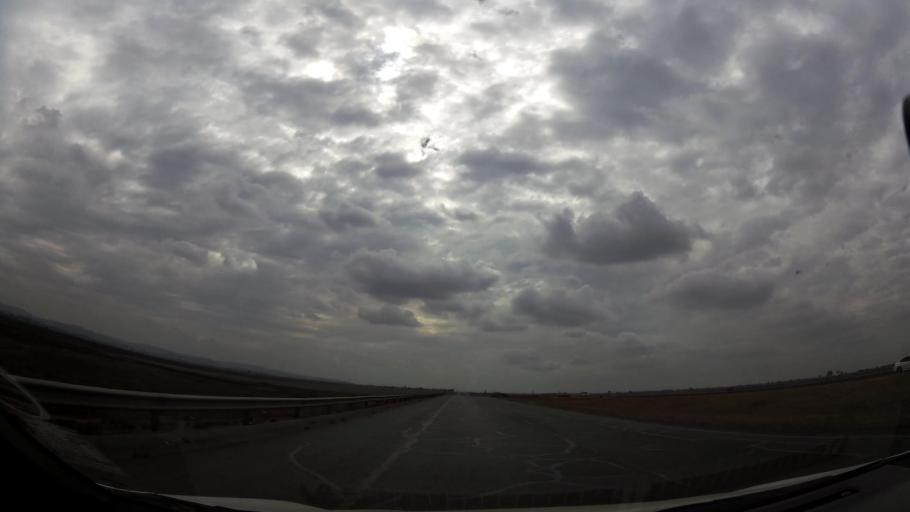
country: ZA
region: Gauteng
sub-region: Ekurhuleni Metropolitan Municipality
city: Germiston
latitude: -26.3811
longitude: 28.0878
